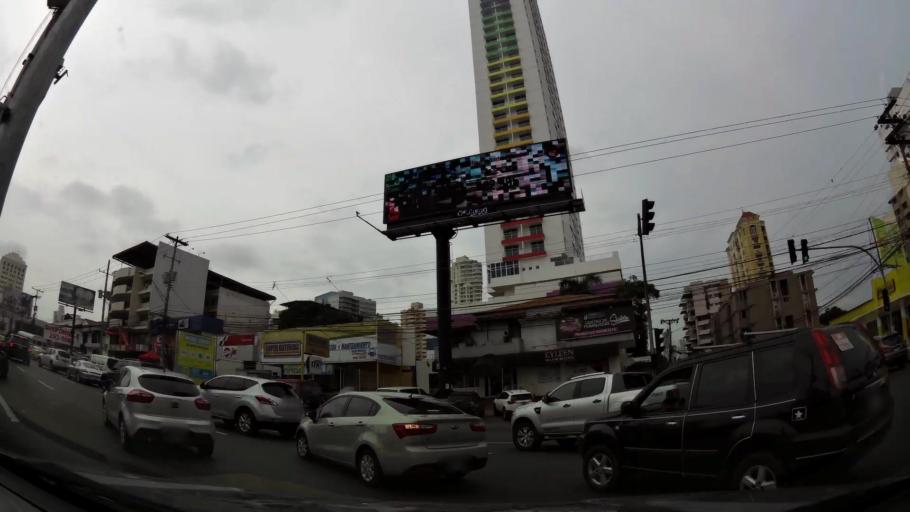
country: PA
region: Panama
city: Panama
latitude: 8.9934
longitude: -79.5198
